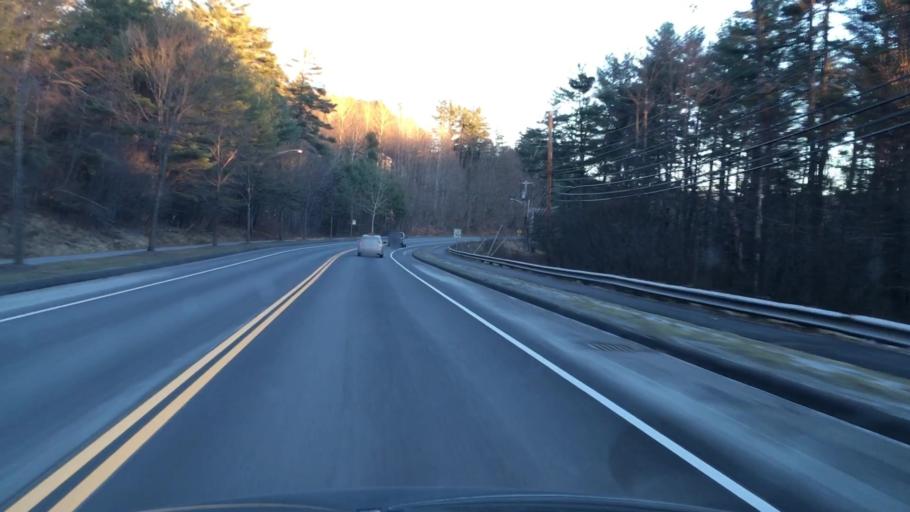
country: US
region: New Hampshire
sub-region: Grafton County
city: Hanover
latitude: 43.6935
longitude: -72.2746
